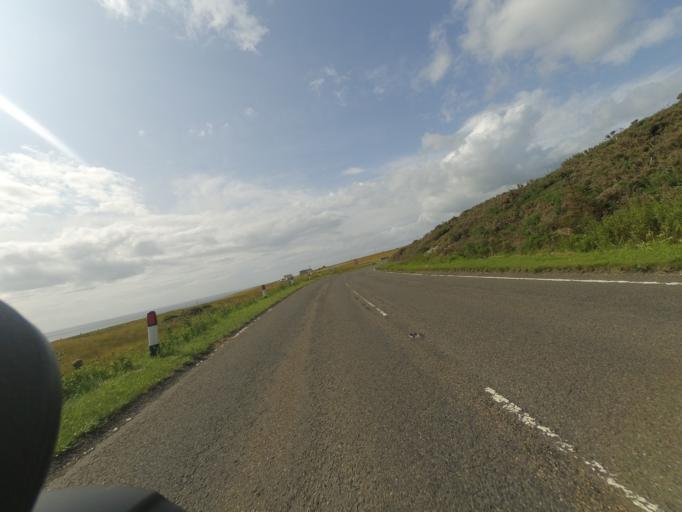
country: GB
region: Scotland
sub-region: Highland
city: Wick
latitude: 58.3260
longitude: -3.1949
